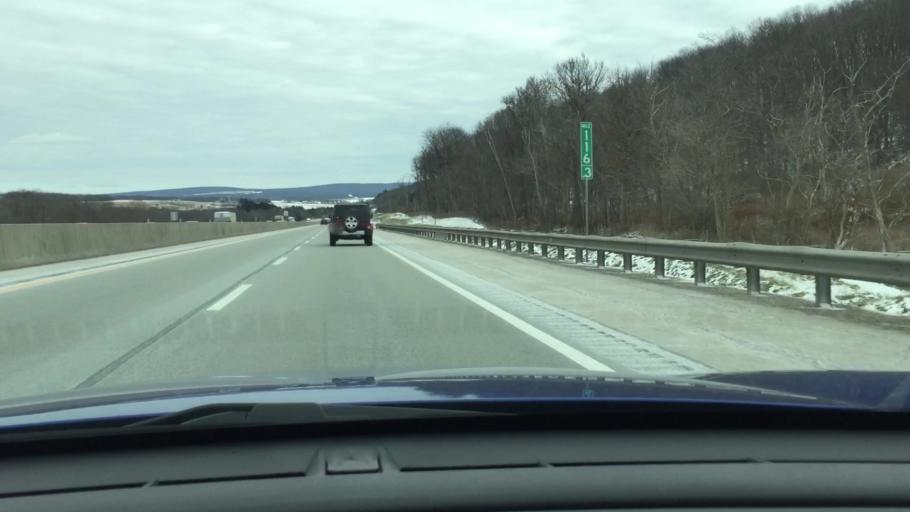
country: US
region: Pennsylvania
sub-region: Somerset County
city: Friedens
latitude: 39.9875
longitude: -78.9740
